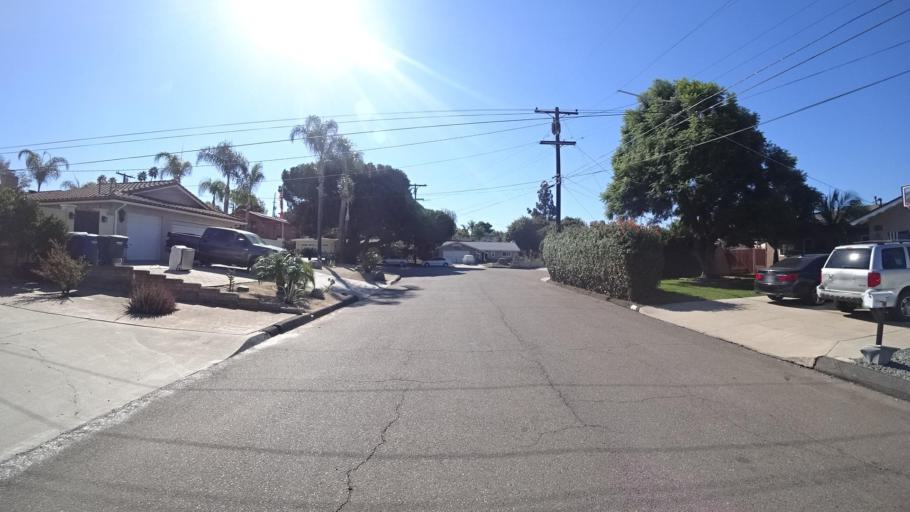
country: US
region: California
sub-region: San Diego County
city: Bonita
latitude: 32.6729
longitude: -117.0184
